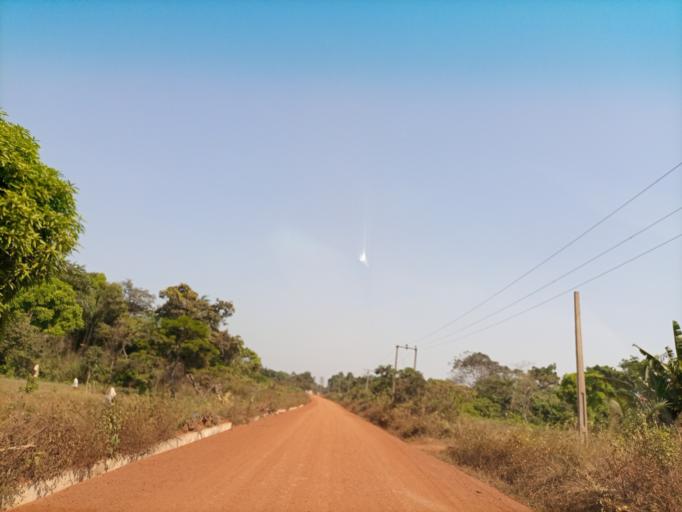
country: NG
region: Enugu
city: Nsukka
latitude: 6.7993
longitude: 7.3472
